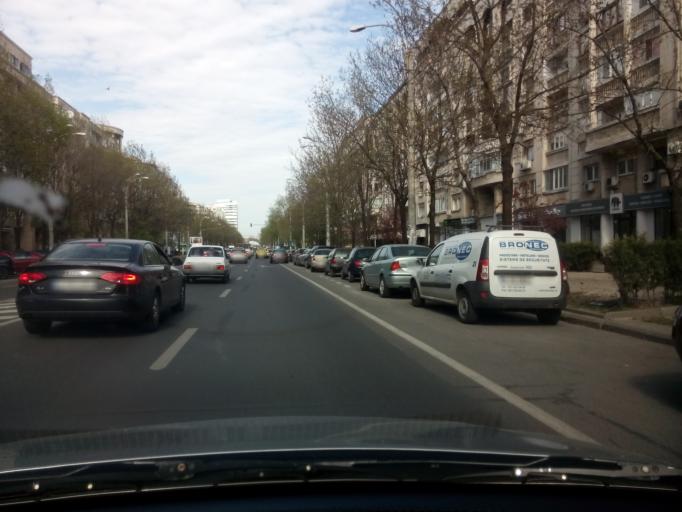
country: RO
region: Bucuresti
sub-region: Municipiul Bucuresti
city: Bucharest
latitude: 44.4275
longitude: 26.1311
